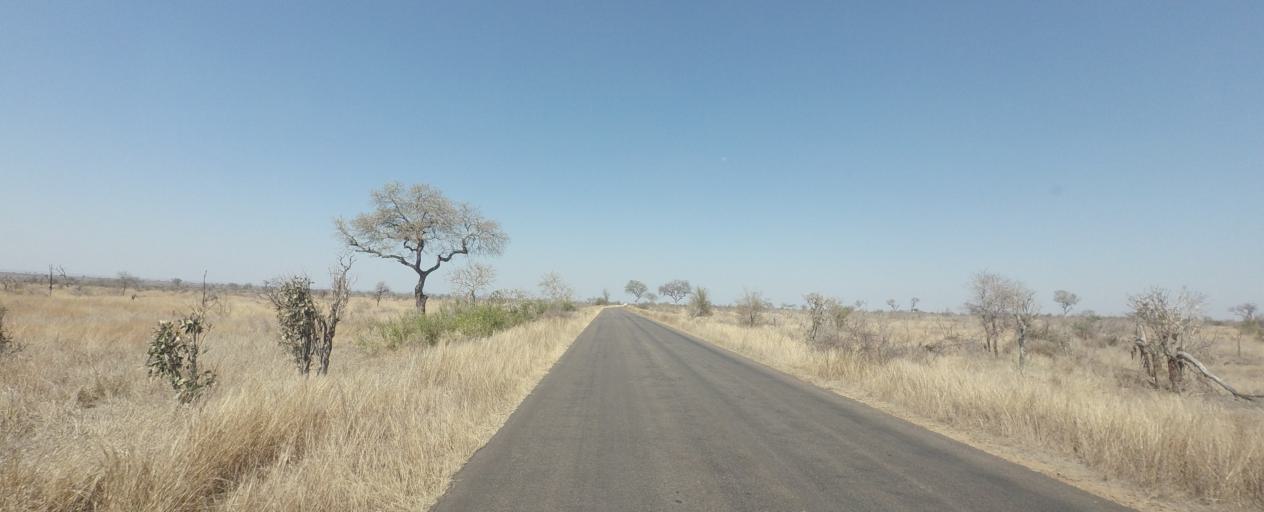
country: ZA
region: Limpopo
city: Thulamahashi
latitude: -24.3972
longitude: 31.7427
